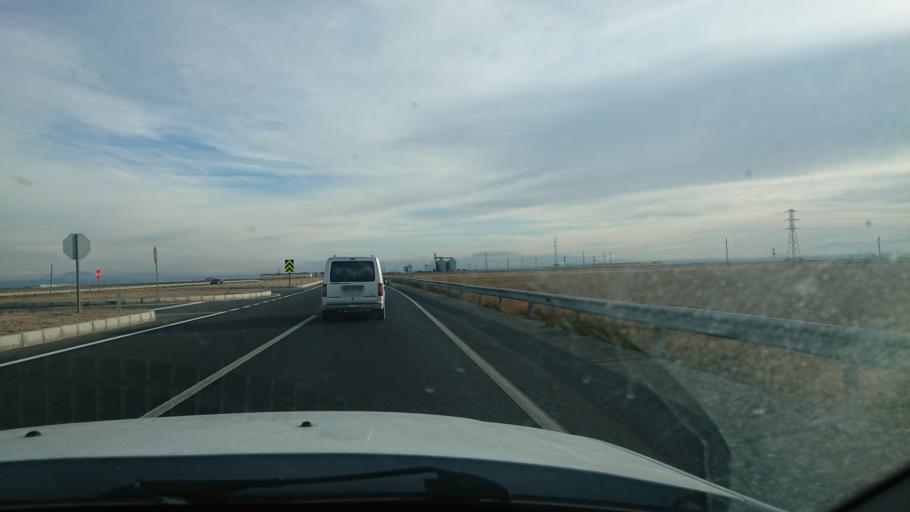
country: TR
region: Aksaray
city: Yesilova
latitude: 38.3042
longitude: 33.8095
